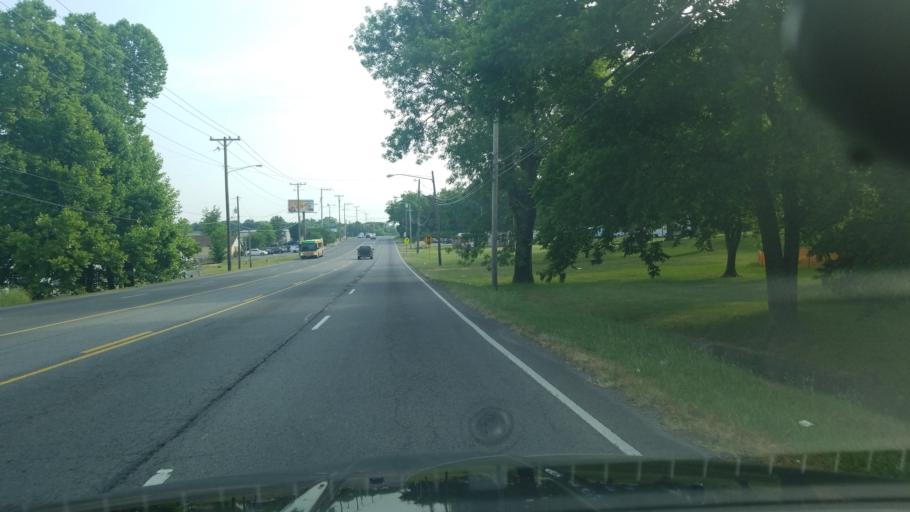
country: US
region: Tennessee
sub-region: Davidson County
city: Goodlettsville
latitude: 36.2753
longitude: -86.7524
